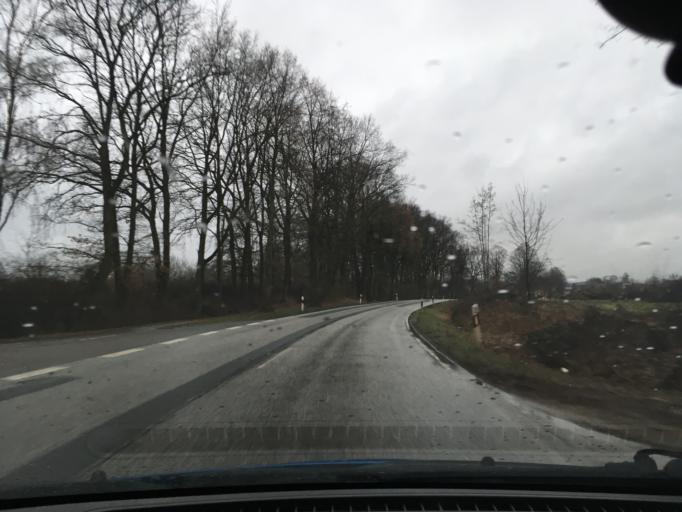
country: DE
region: Schleswig-Holstein
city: Wiershop
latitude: 53.4030
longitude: 10.4491
